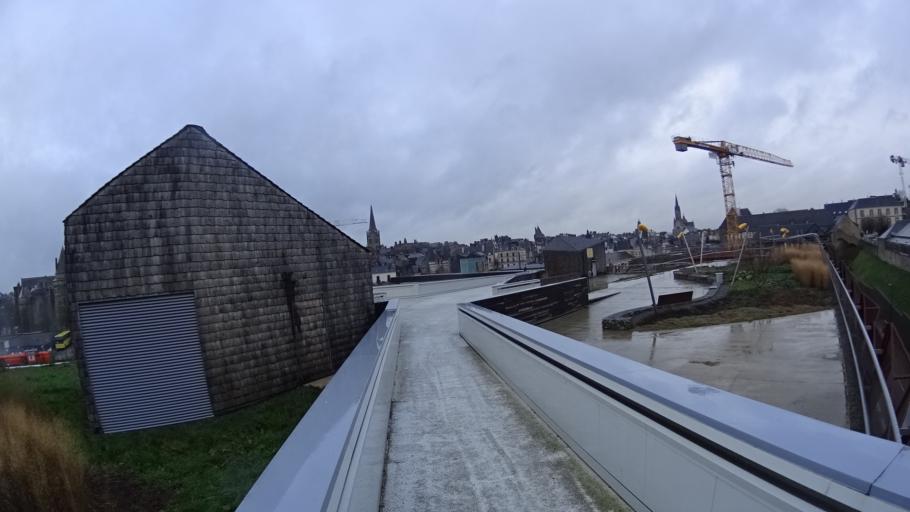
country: FR
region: Brittany
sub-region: Departement d'Ille-et-Vilaine
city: Vitre
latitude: 48.1218
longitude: -1.2142
